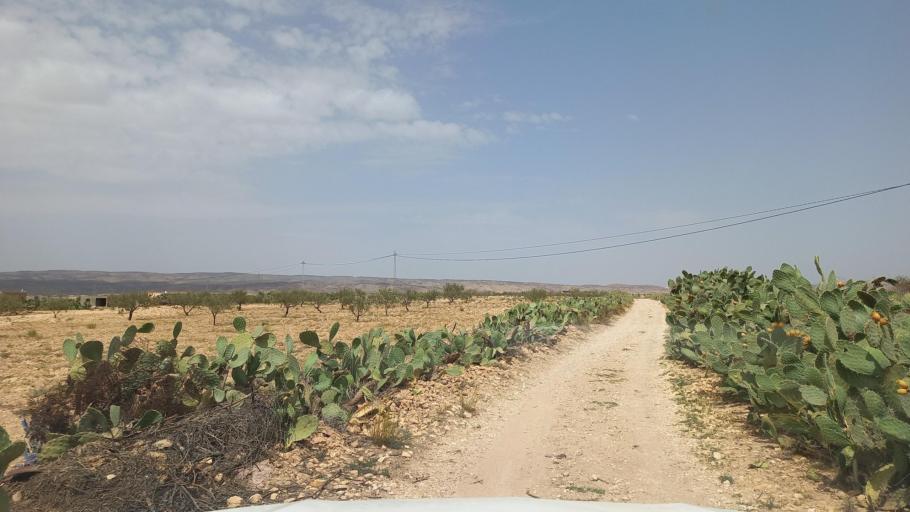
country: TN
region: Al Qasrayn
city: Kasserine
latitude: 35.2879
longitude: 9.0060
